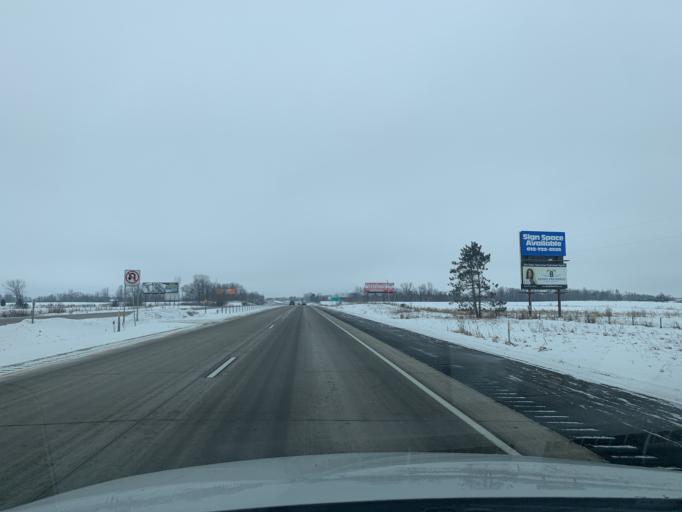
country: US
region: Minnesota
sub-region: Pine County
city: Rock Creek
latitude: 45.7567
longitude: -92.9911
